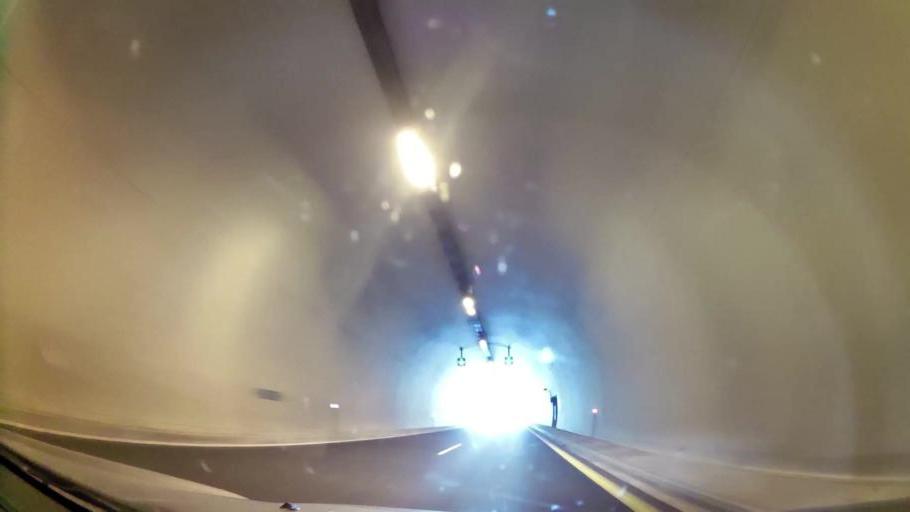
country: GR
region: Central Macedonia
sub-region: Nomos Imathias
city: Rizomata
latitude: 40.3803
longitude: 22.1012
